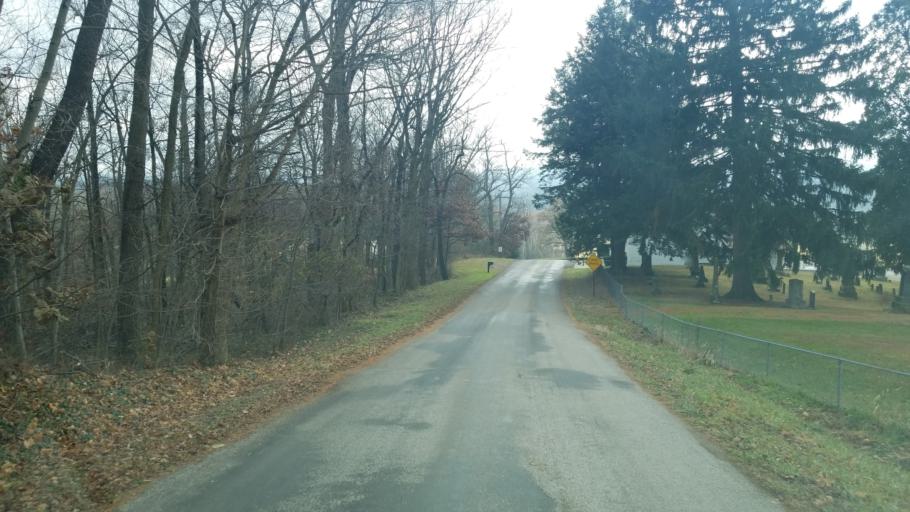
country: US
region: Ohio
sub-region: Richland County
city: Lincoln Heights
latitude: 40.8252
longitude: -82.4421
